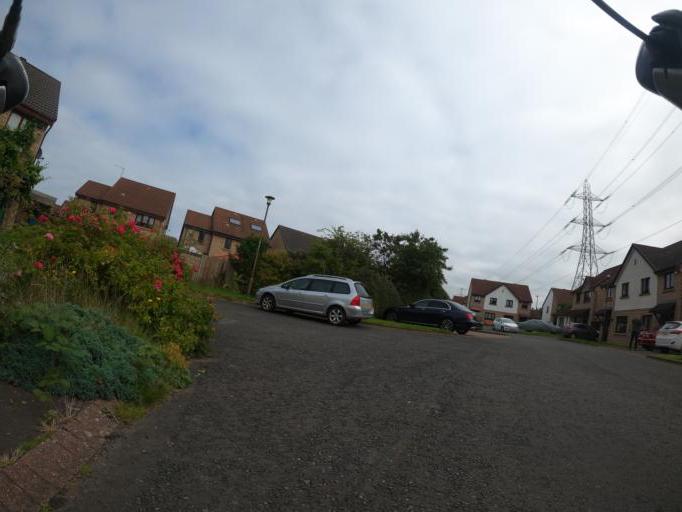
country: GB
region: Scotland
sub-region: East Lothian
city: Musselburgh
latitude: 55.9388
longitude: -3.0954
